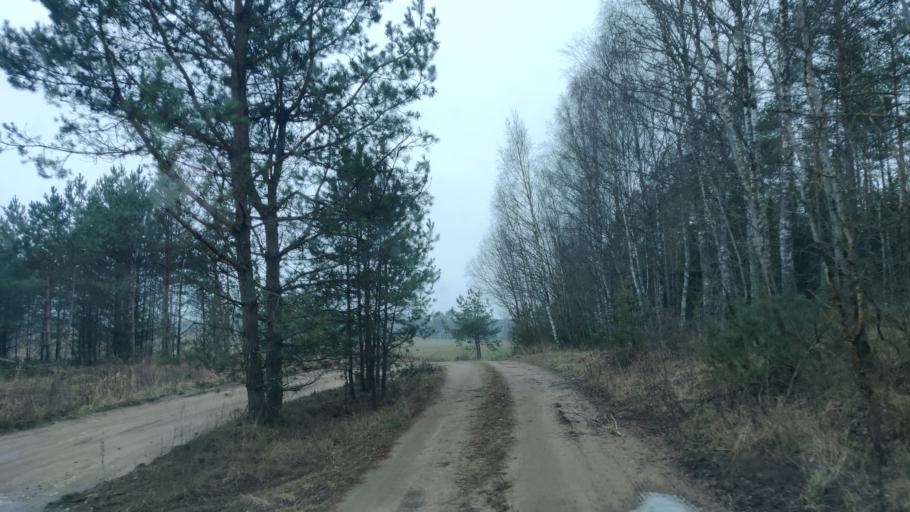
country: LT
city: Trakai
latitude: 54.5534
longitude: 24.9500
